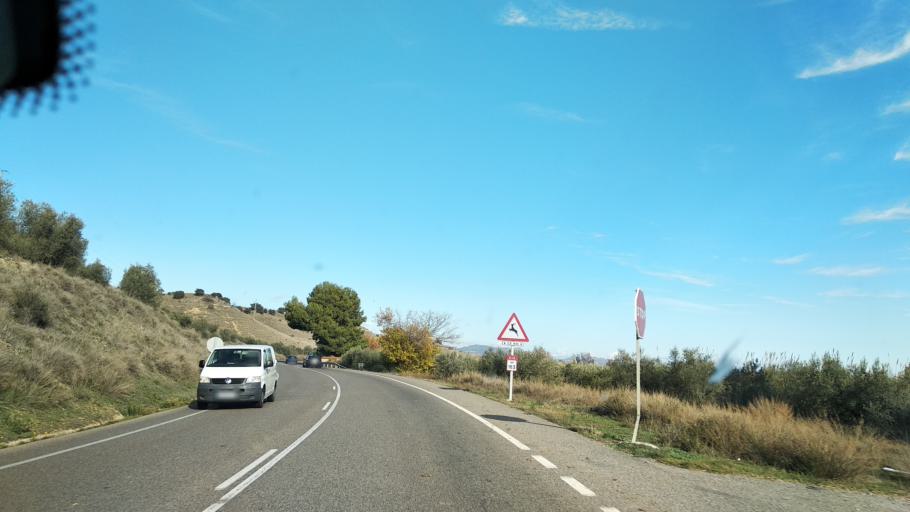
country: ES
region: Catalonia
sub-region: Provincia de Lleida
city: Vallfogona de Balaguer
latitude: 41.7588
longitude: 0.7738
